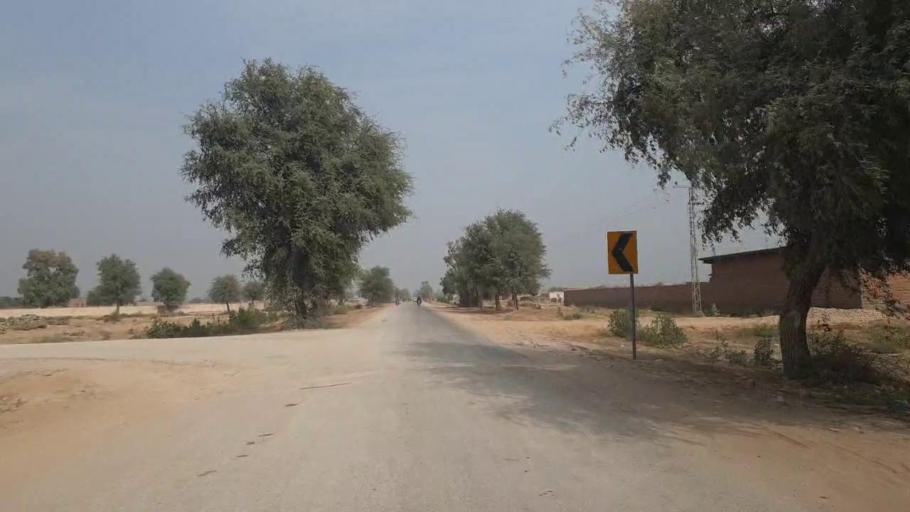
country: PK
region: Sindh
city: Sann
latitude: 26.0315
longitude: 68.1279
